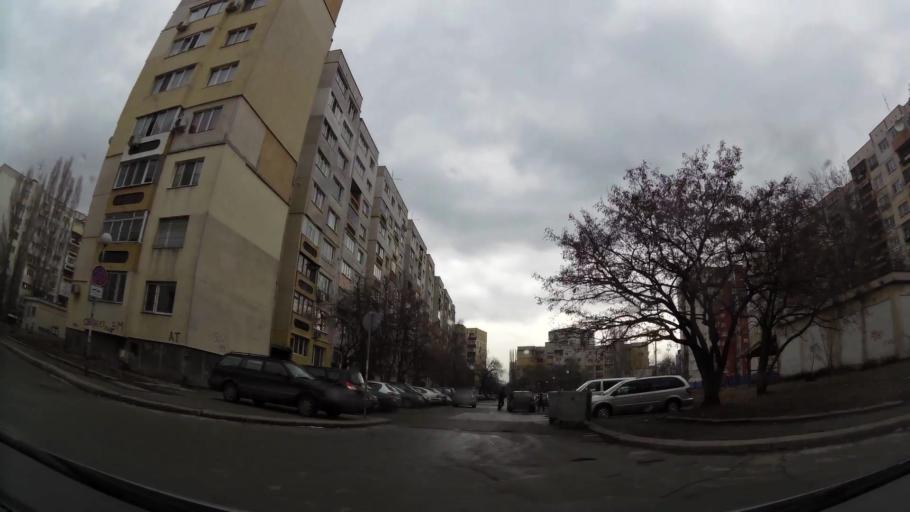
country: BG
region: Sofia-Capital
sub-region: Stolichna Obshtina
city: Sofia
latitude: 42.7291
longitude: 23.2981
